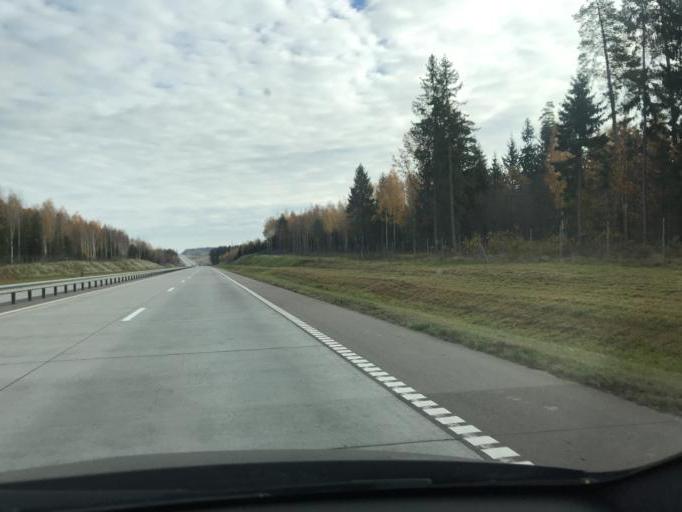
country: BY
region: Minsk
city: Zaslawye
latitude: 54.0642
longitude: 27.3261
